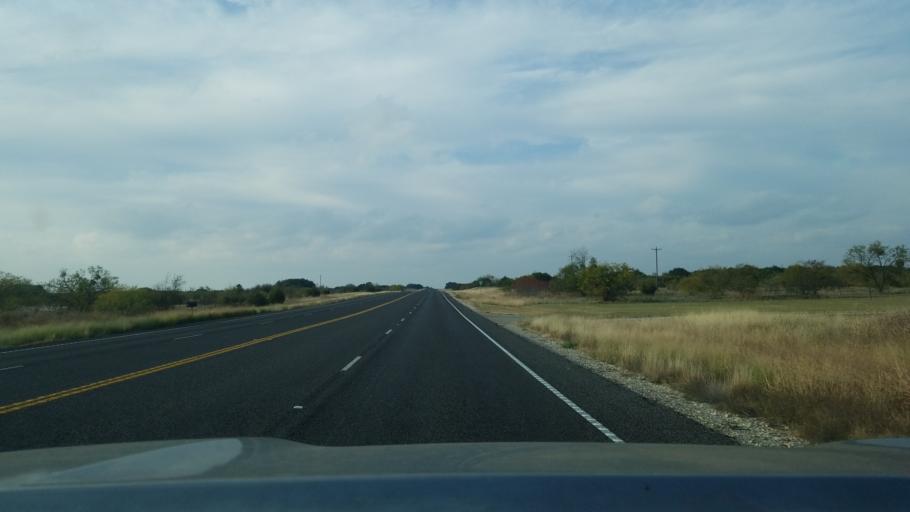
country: US
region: Texas
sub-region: Mills County
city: Goldthwaite
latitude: 31.3074
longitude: -98.4787
